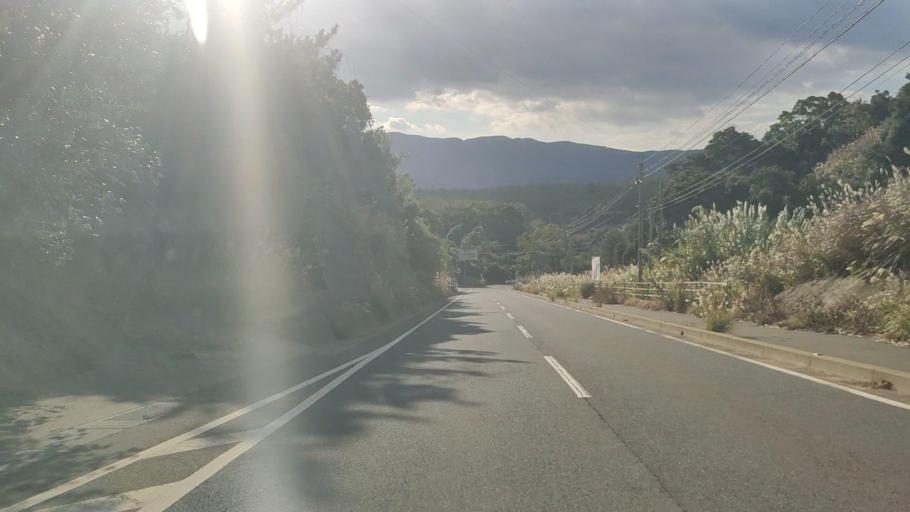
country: JP
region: Kagoshima
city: Tarumizu
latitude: 31.5953
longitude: 130.7085
